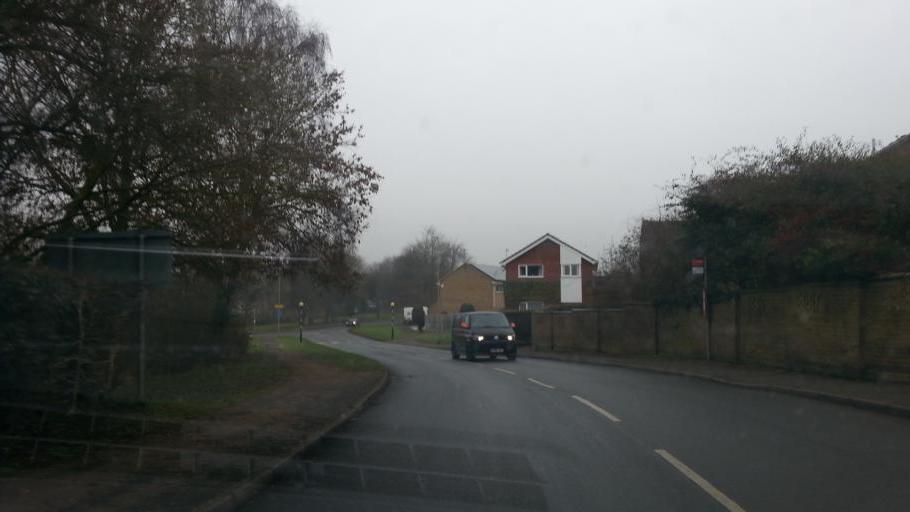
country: GB
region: England
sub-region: Northamptonshire
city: Brackley
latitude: 52.0314
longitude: -1.1604
